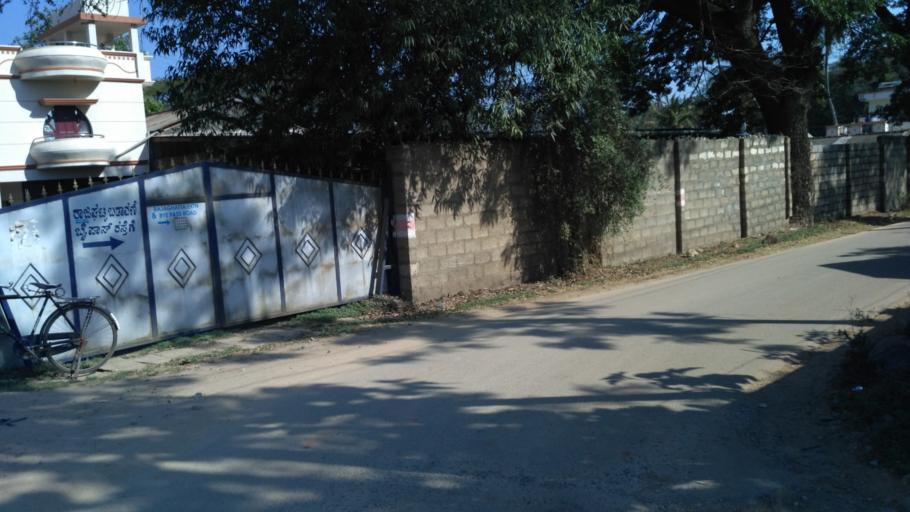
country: IN
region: Karnataka
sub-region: Hassan
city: Hassan
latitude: 13.0023
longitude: 76.1160
